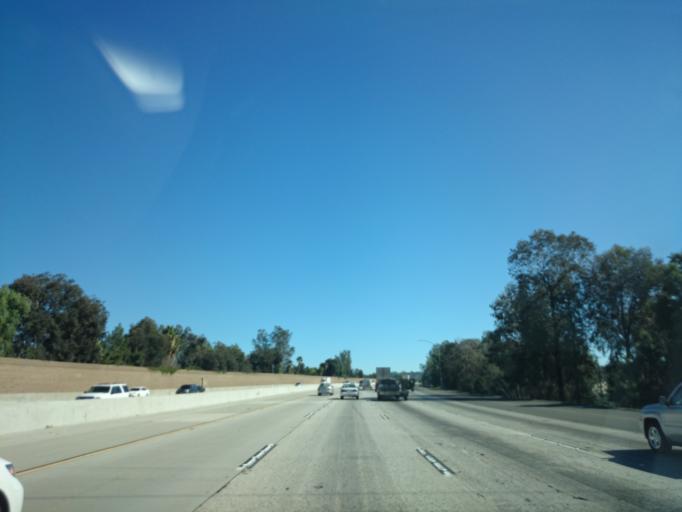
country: US
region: California
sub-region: San Bernardino County
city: Redlands
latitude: 34.0611
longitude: -117.1766
